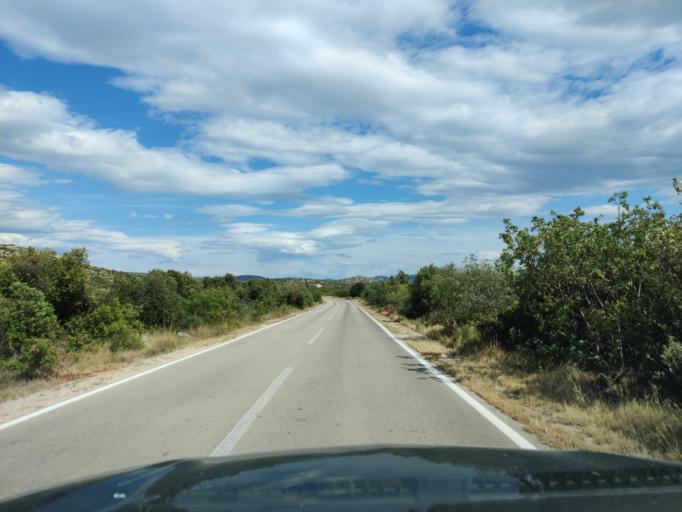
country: HR
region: Sibensko-Kniniska
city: Zaton
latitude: 43.7425
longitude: 15.8528
